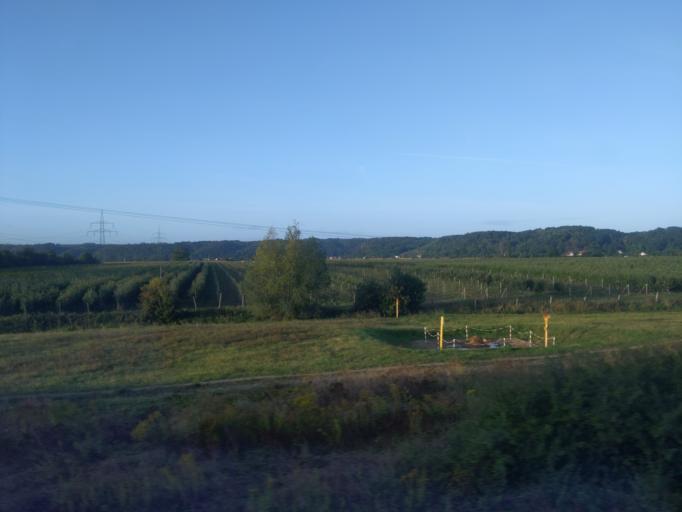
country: DE
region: Saxony
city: Niederau
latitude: 51.1547
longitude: 13.5362
